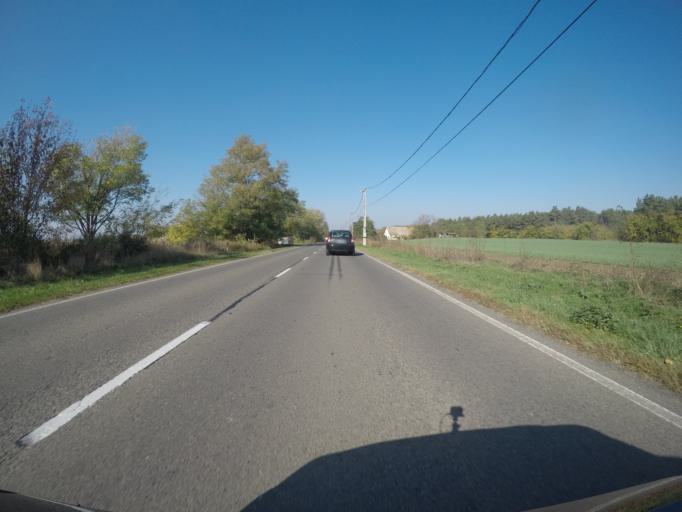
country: HU
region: Tolna
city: Szedres
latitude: 46.5061
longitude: 18.6678
